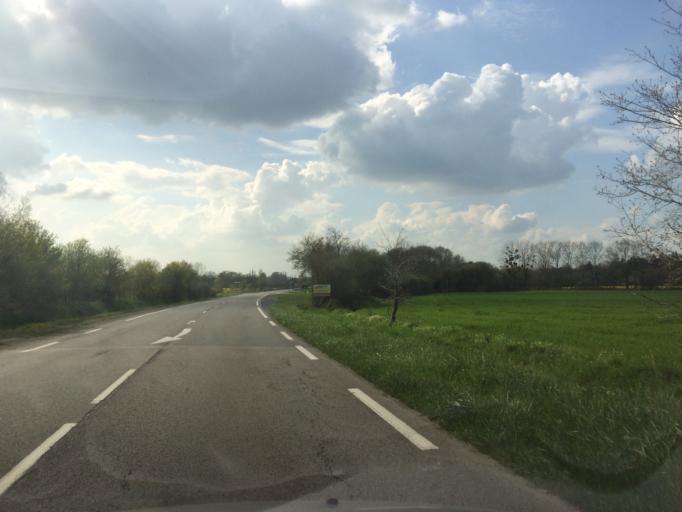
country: FR
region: Pays de la Loire
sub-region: Departement de la Loire-Atlantique
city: Blain
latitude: 47.4669
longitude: -1.7151
